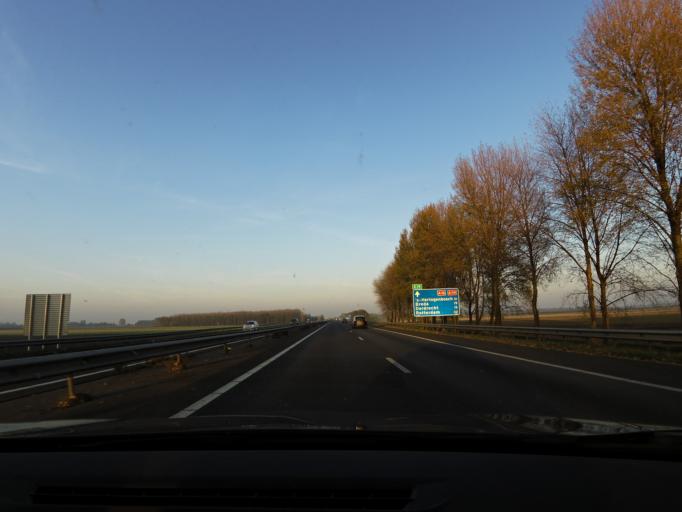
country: NL
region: North Brabant
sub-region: Gemeente Moerdijk
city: Klundert
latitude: 51.6851
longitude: 4.6297
